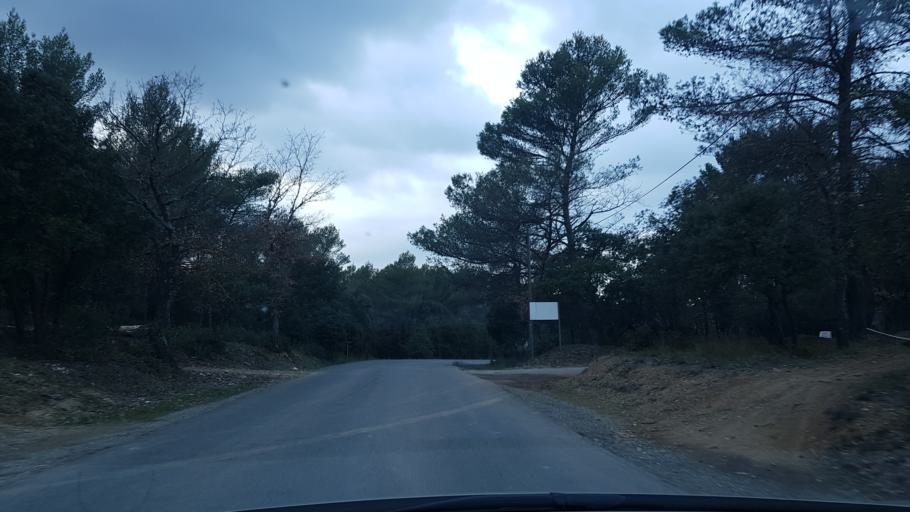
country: FR
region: Provence-Alpes-Cote d'Azur
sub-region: Departement des Bouches-du-Rhone
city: Mimet
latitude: 43.4306
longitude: 5.5088
